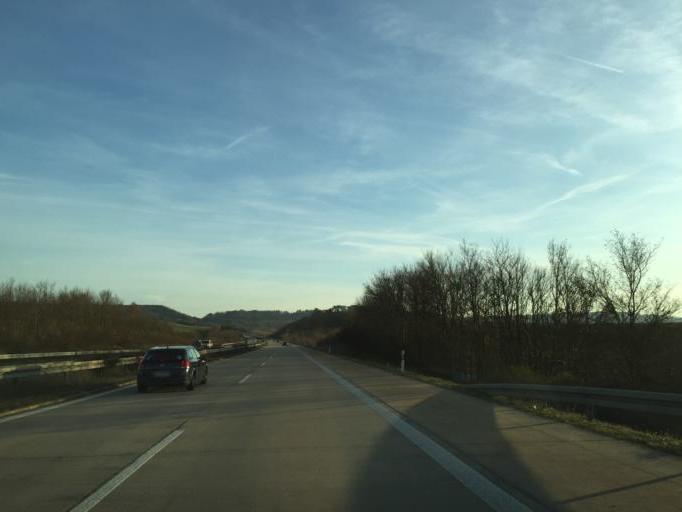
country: DE
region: Bavaria
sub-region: Regierungsbezirk Mittelfranken
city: Diebach
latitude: 49.3020
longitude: 10.2109
